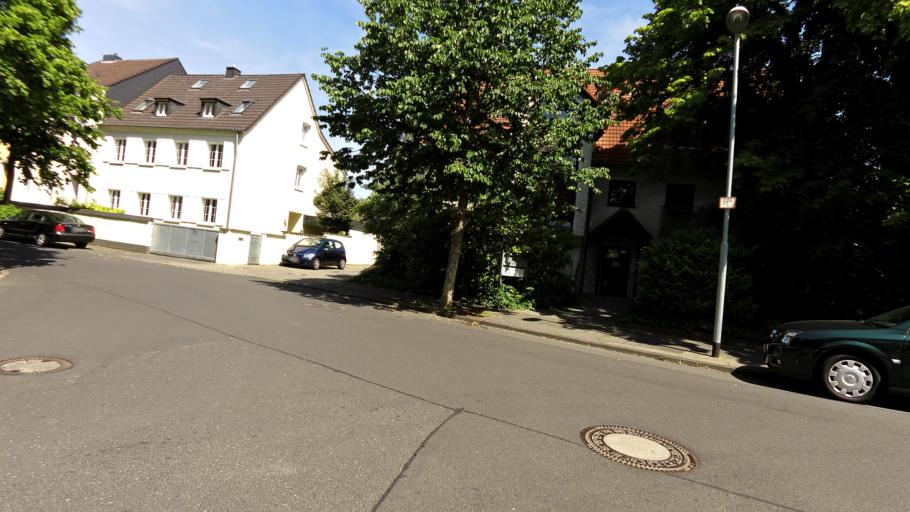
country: DE
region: North Rhine-Westphalia
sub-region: Regierungsbezirk Koln
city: Rheinbach
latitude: 50.6282
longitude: 6.9503
